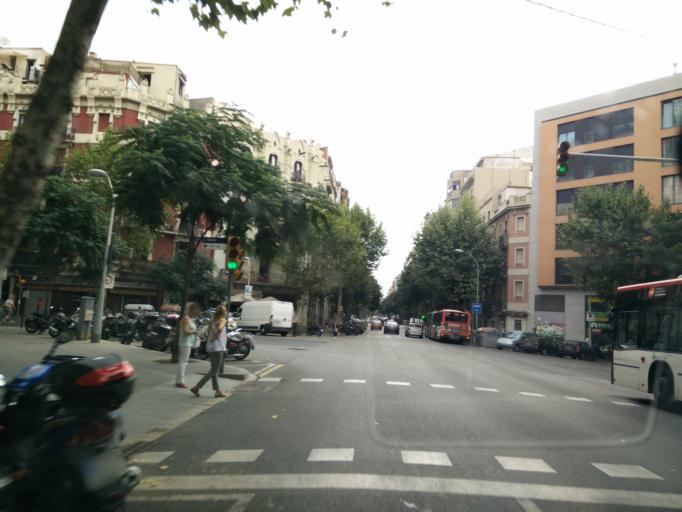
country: ES
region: Catalonia
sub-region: Provincia de Barcelona
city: Horta-Guinardo
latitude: 41.4024
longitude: 2.1766
